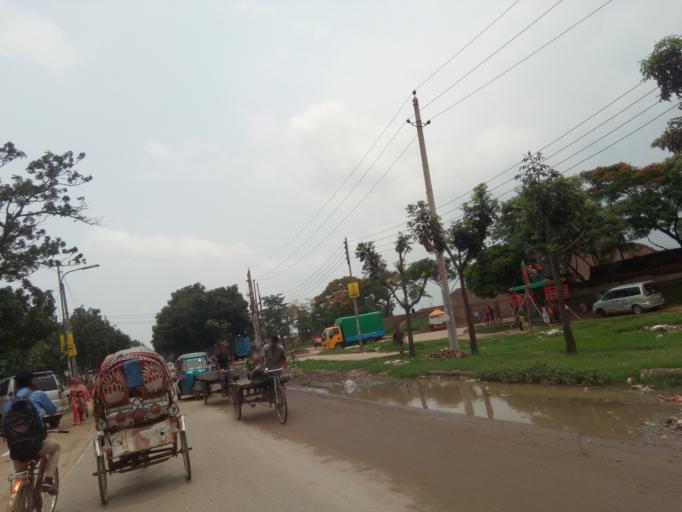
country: BD
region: Dhaka
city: Azimpur
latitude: 23.7519
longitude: 90.3577
